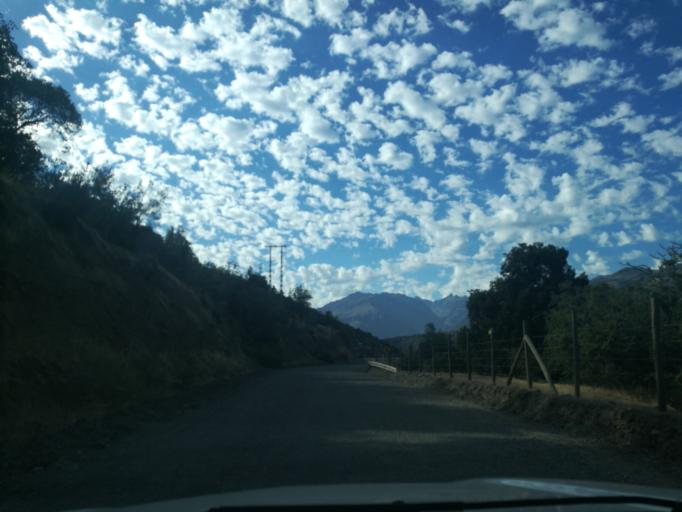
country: CL
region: O'Higgins
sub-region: Provincia de Cachapoal
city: Machali
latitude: -34.2690
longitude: -70.4554
